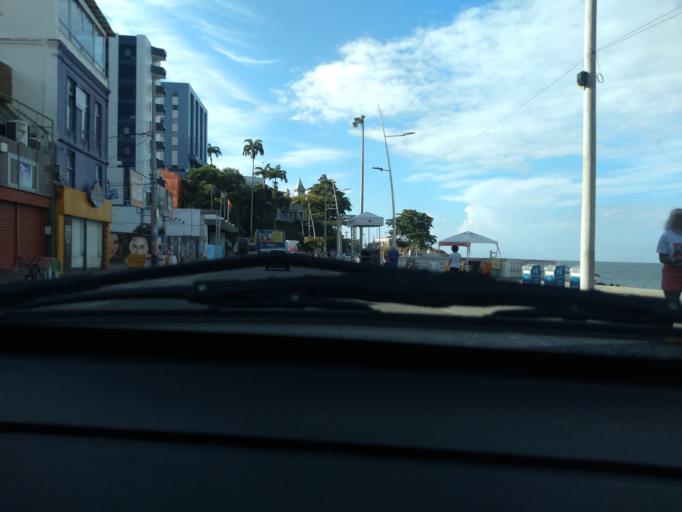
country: BR
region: Bahia
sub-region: Salvador
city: Salvador
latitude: -13.0048
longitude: -38.5332
